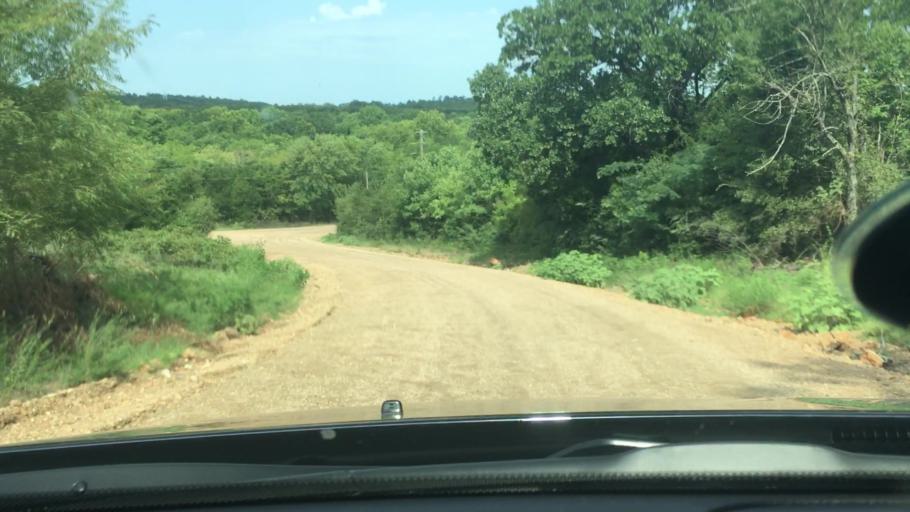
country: US
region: Oklahoma
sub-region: Atoka County
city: Atoka
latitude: 34.4411
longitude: -96.0653
